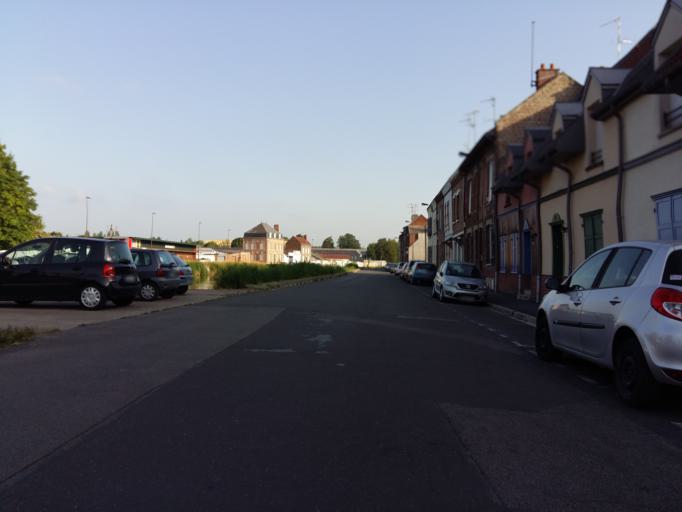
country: FR
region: Picardie
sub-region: Departement de la Somme
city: Amiens
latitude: 49.9002
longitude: 2.2892
